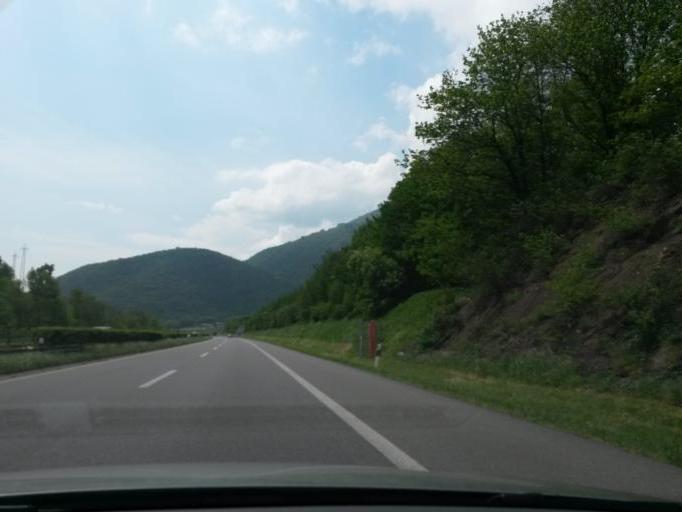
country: CH
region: Ticino
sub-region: Lugano District
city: Gravesano
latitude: 46.0895
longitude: 8.9231
